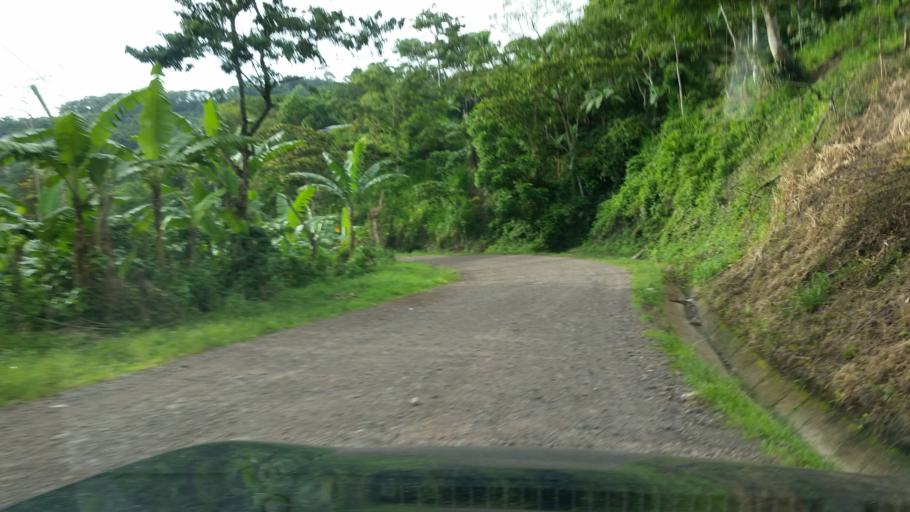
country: NI
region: Jinotega
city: Jinotega
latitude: 13.2474
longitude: -85.7321
